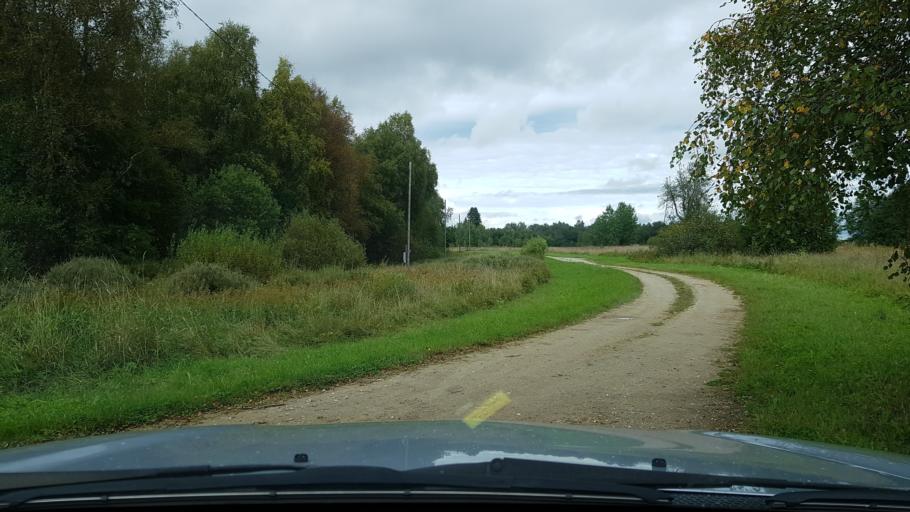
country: EE
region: Harju
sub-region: Raasiku vald
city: Arukula
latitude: 59.3599
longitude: 25.0038
